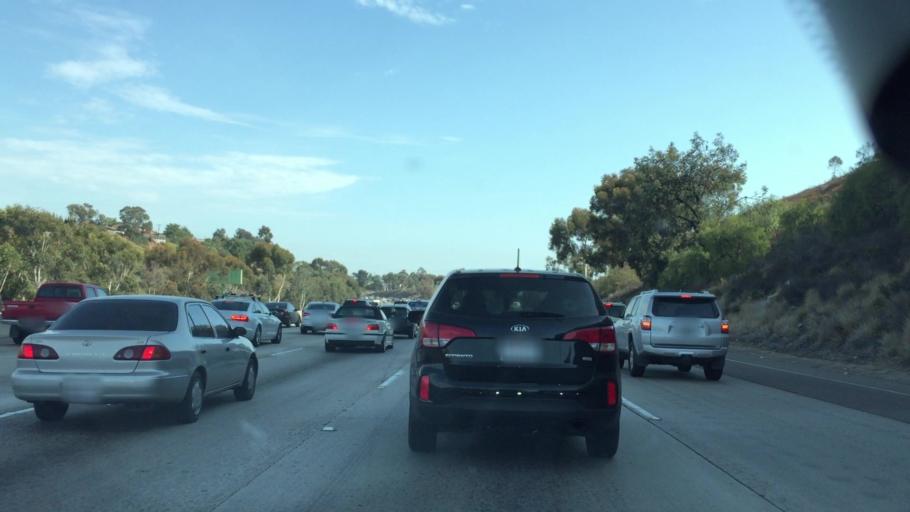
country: US
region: California
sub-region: San Diego County
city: San Diego
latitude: 32.7968
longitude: -117.1497
